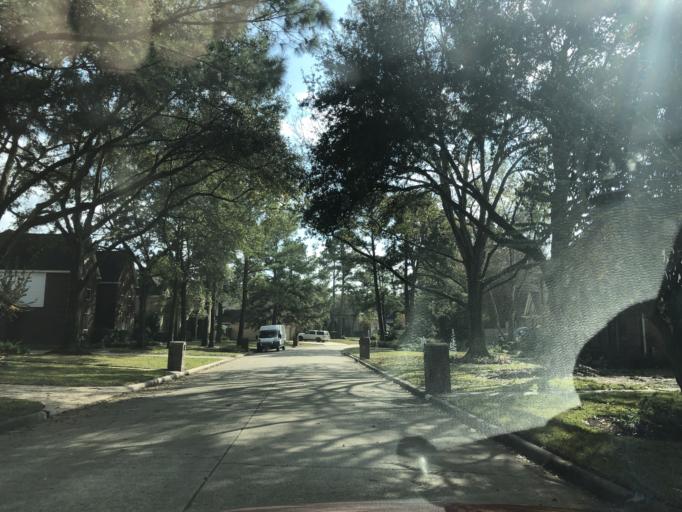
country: US
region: Texas
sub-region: Harris County
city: Tomball
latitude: 30.0234
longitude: -95.5460
